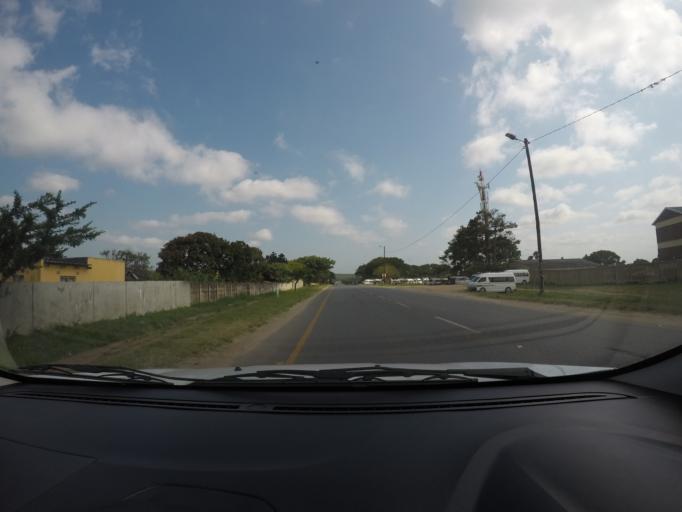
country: ZA
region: KwaZulu-Natal
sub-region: uThungulu District Municipality
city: eSikhawini
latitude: -28.8814
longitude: 31.9029
